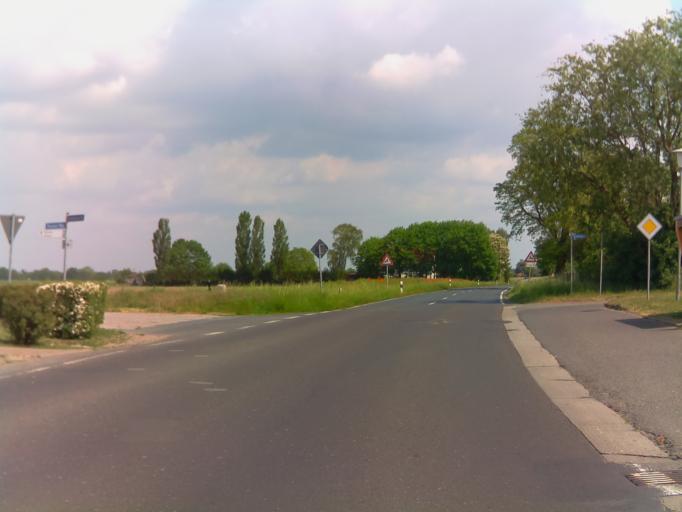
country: DE
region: Brandenburg
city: Retzow
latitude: 52.6270
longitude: 12.6838
